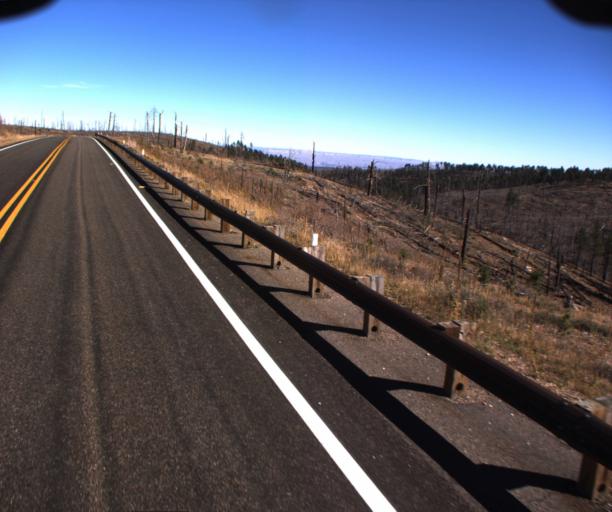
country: US
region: Arizona
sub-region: Coconino County
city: Fredonia
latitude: 36.6157
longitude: -112.1819
